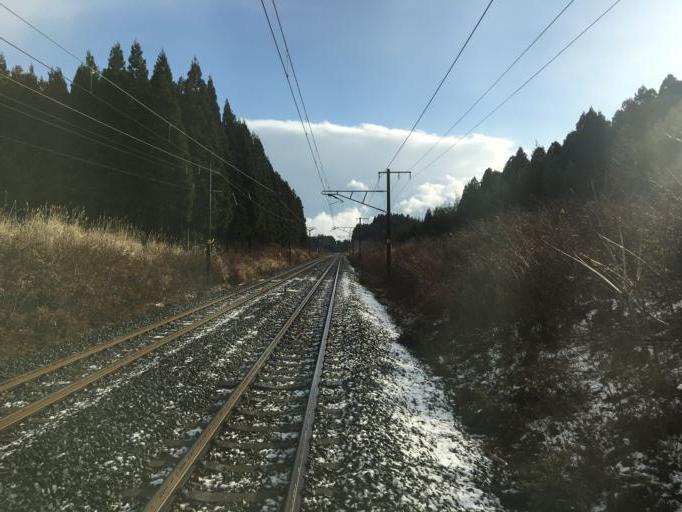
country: JP
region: Aomori
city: Aomori Shi
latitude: 40.9092
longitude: 141.0543
